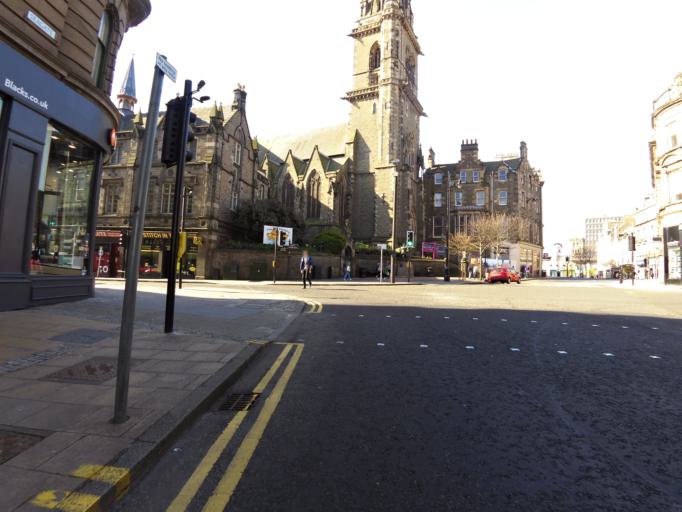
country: GB
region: Scotland
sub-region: Dundee City
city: Dundee
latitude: 56.4615
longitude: -2.9680
